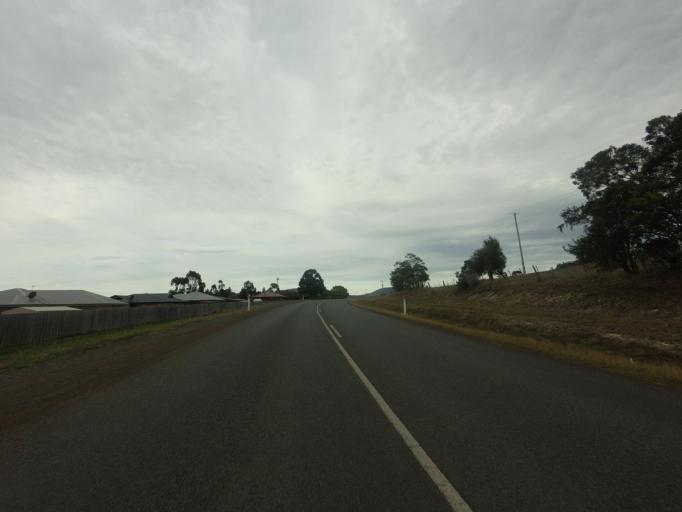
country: AU
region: Tasmania
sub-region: Brighton
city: Bridgewater
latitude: -42.7007
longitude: 147.2382
